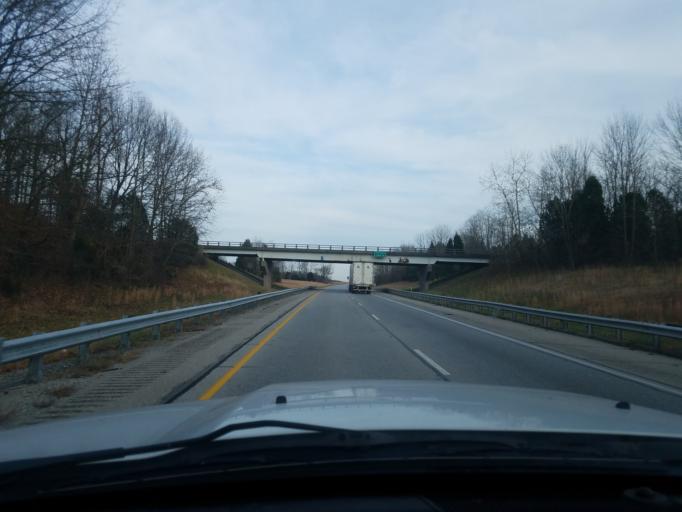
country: US
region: Indiana
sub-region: Harrison County
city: Corydon
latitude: 38.2509
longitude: -86.0522
